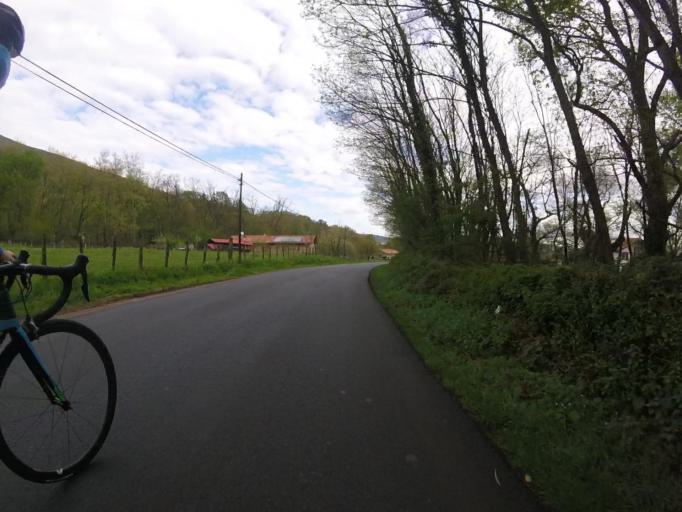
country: FR
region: Aquitaine
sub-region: Departement des Pyrenees-Atlantiques
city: Sare
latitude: 43.3038
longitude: -1.5929
